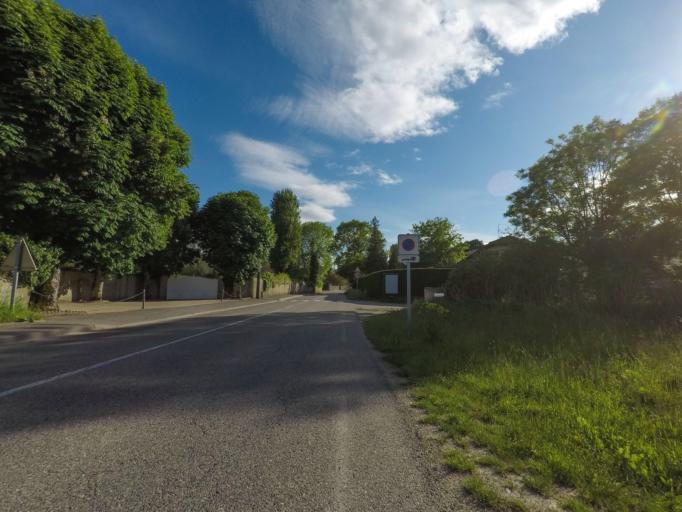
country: FR
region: Rhone-Alpes
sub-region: Departement de l'Ain
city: Saint-Genis-Pouilly
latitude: 46.2565
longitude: 6.0381
